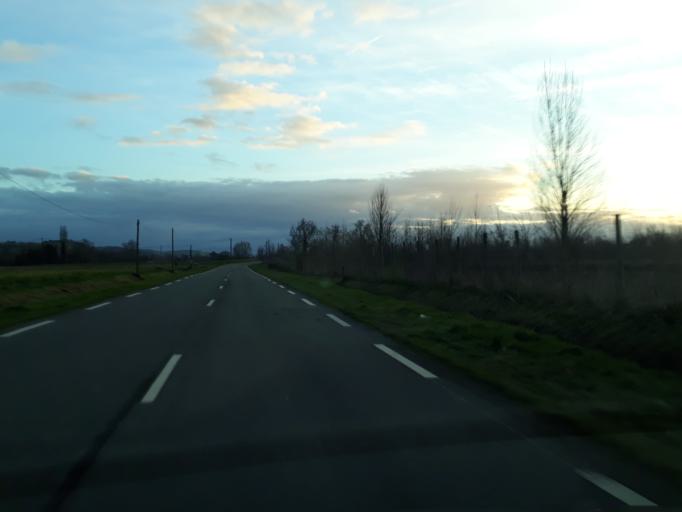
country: FR
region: Midi-Pyrenees
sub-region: Departement de la Haute-Garonne
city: Marquefave
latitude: 43.3322
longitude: 1.2498
